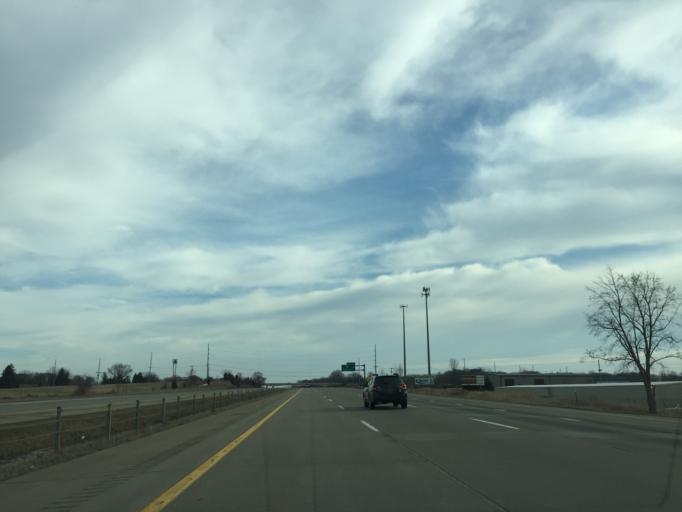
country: US
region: Michigan
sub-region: Berrien County
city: Fair Plain
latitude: 42.0570
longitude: -86.4652
